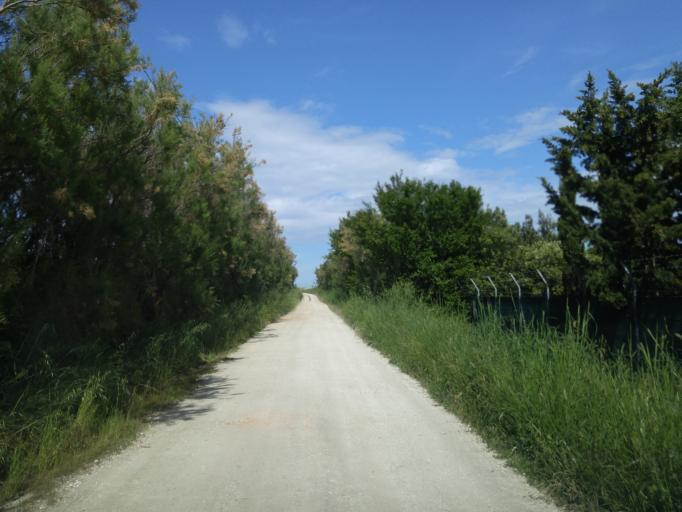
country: IT
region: The Marches
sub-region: Provincia di Pesaro e Urbino
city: San Costanzo
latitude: 43.7896
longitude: 13.0582
